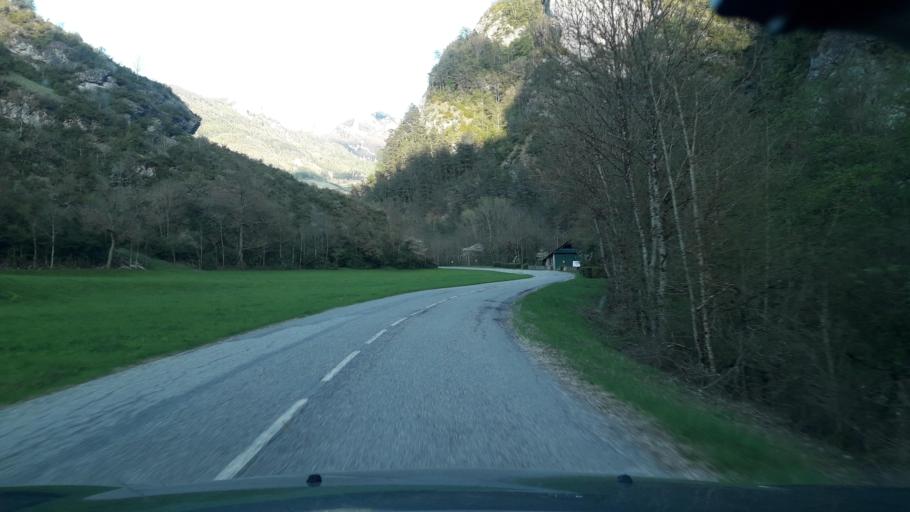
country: FR
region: Rhone-Alpes
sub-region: Departement de l'Isere
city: Mens
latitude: 44.6847
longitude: 5.5916
